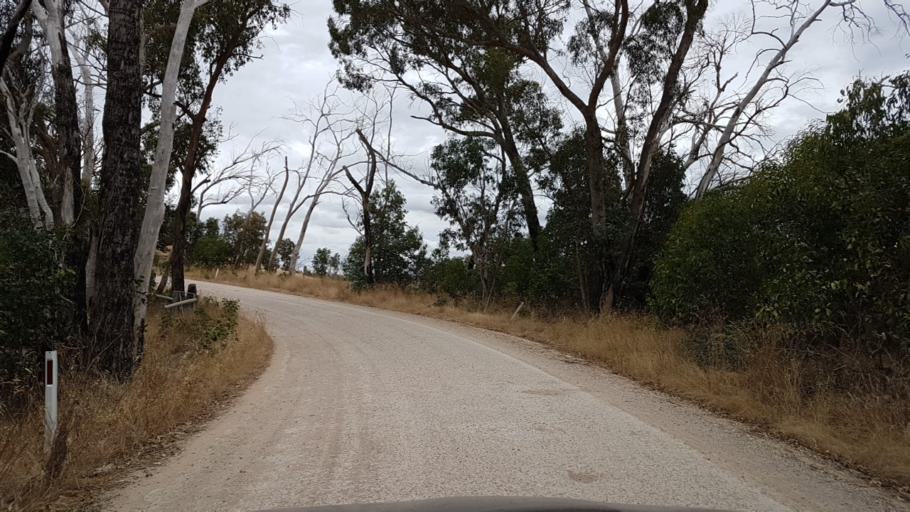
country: AU
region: South Australia
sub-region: Adelaide Hills
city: Gumeracha
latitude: -34.8002
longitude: 138.8138
